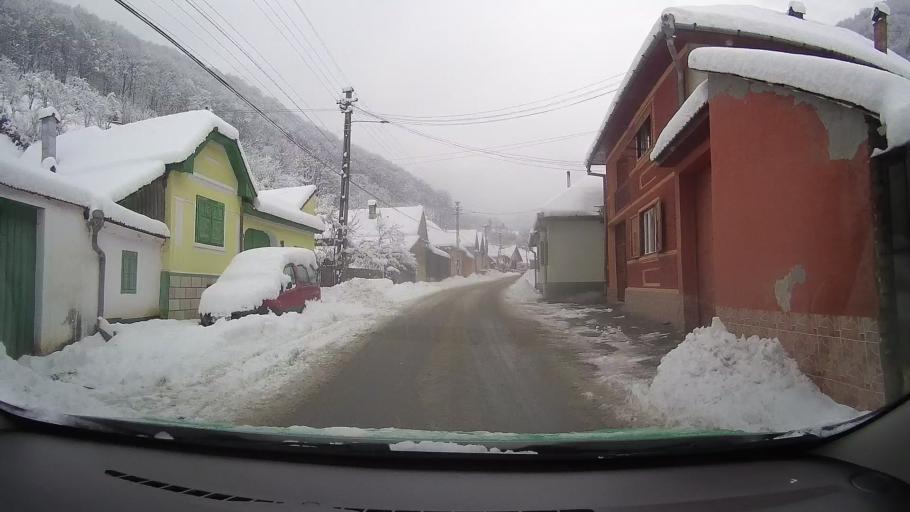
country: RO
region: Alba
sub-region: Comuna Sugag
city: Dobra
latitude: 45.7598
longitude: 23.6612
